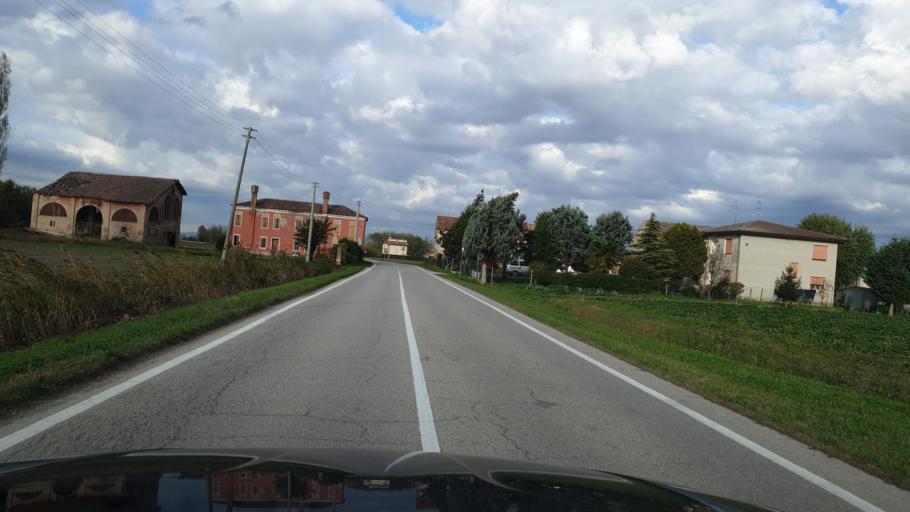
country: IT
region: Veneto
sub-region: Provincia di Rovigo
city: Villanova del Ghebbo Canton
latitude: 45.0647
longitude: 11.6301
